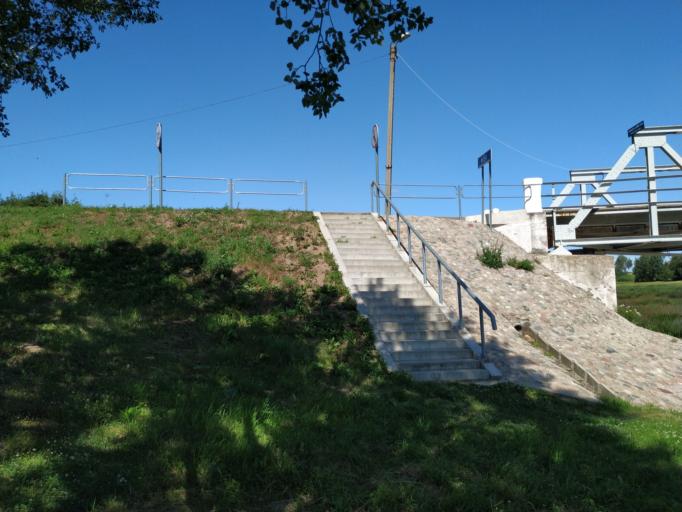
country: LT
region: Panevezys
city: Pasvalys
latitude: 56.2285
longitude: 24.4063
